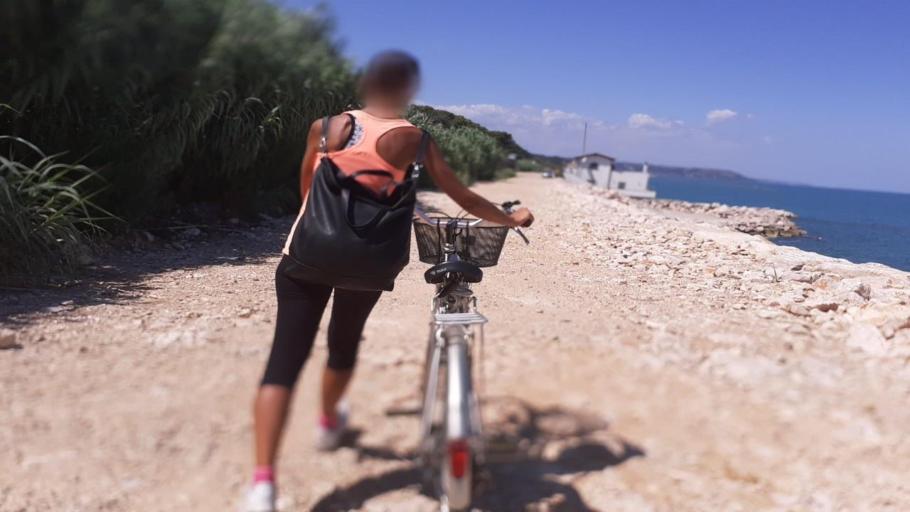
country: IT
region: Abruzzo
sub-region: Provincia di Chieti
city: Torino di Sangro
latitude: 42.2209
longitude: 14.5689
